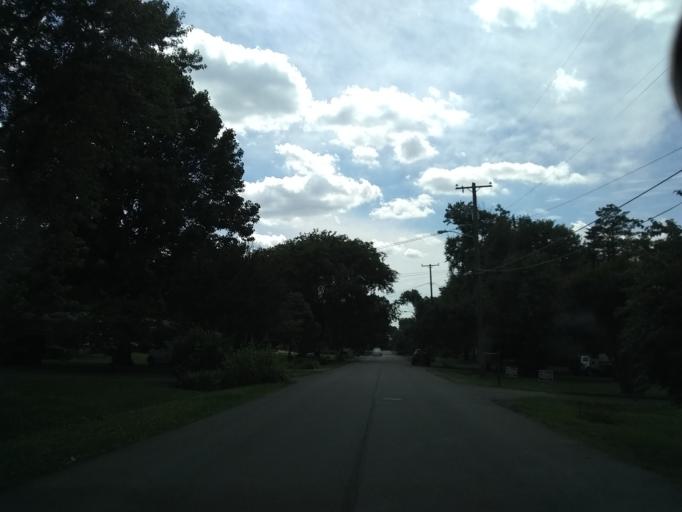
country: US
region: Tennessee
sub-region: Davidson County
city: Nashville
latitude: 36.1521
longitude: -86.6936
